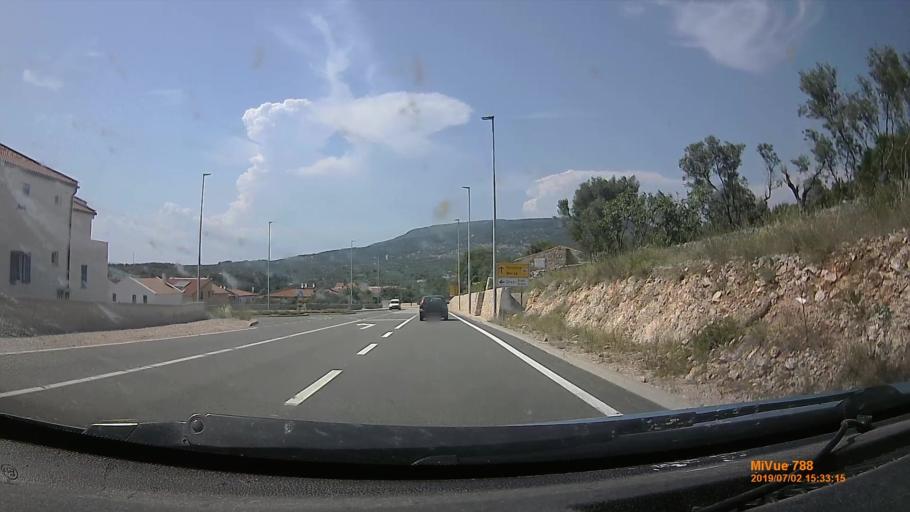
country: HR
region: Primorsko-Goranska
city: Cres
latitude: 44.9581
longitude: 14.4156
